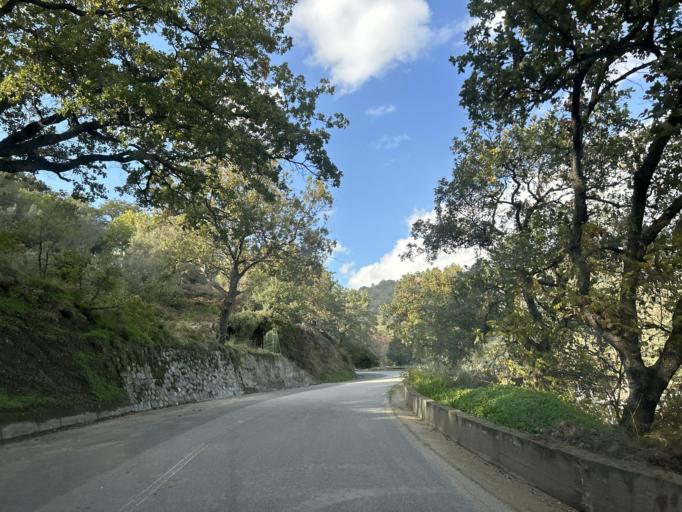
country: IT
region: Calabria
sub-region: Provincia di Catanzaro
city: Montepaone
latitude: 38.7218
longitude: 16.5083
